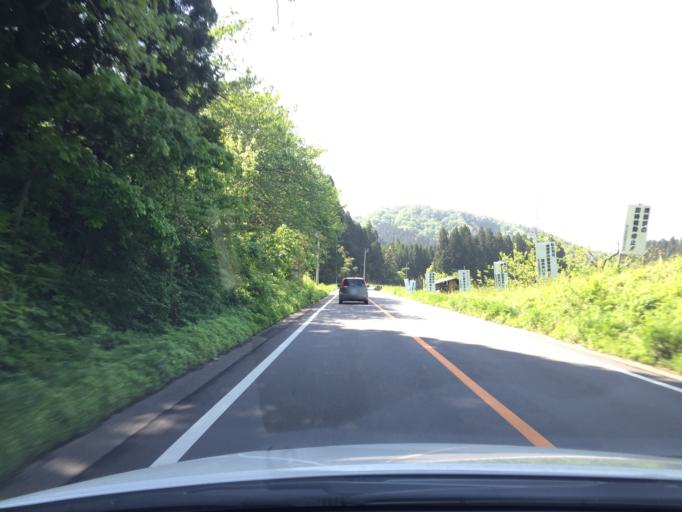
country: JP
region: Niigata
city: Muramatsu
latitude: 37.6606
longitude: 139.1383
